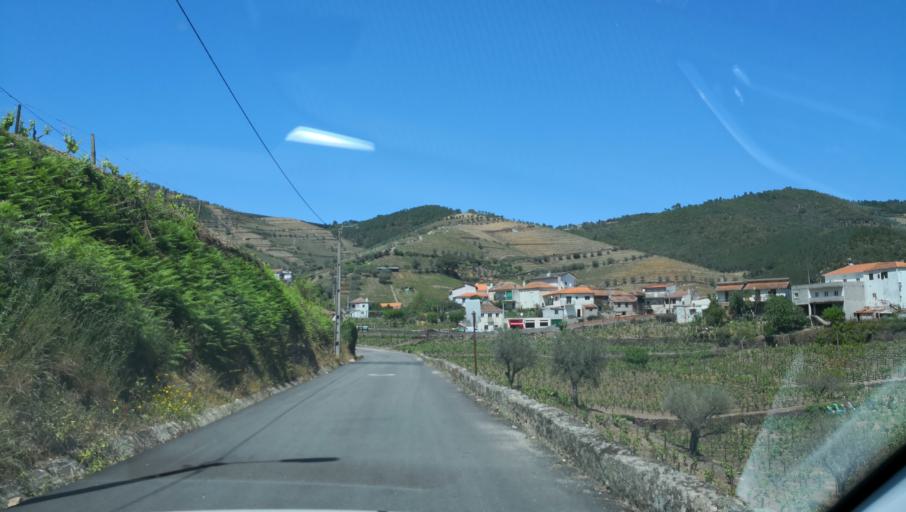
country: PT
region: Vila Real
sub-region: Vila Real
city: Vila Real
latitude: 41.2244
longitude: -7.7203
